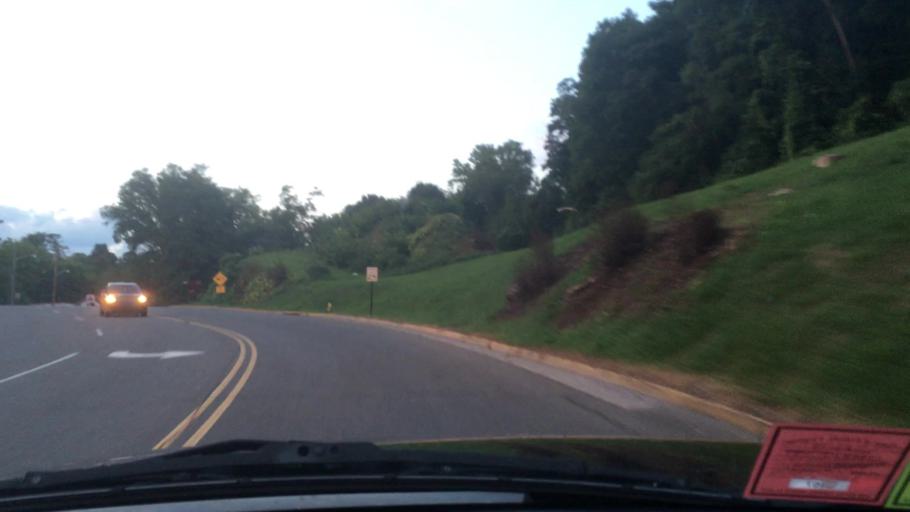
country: US
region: Virginia
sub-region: Pulaski County
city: Pulaski
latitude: 37.0521
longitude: -80.7739
